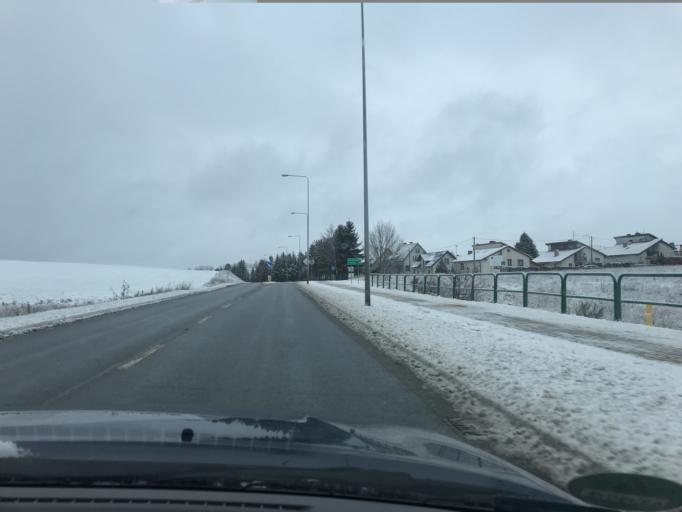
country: PL
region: Pomeranian Voivodeship
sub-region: Powiat bytowski
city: Bytow
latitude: 54.1872
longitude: 17.5091
